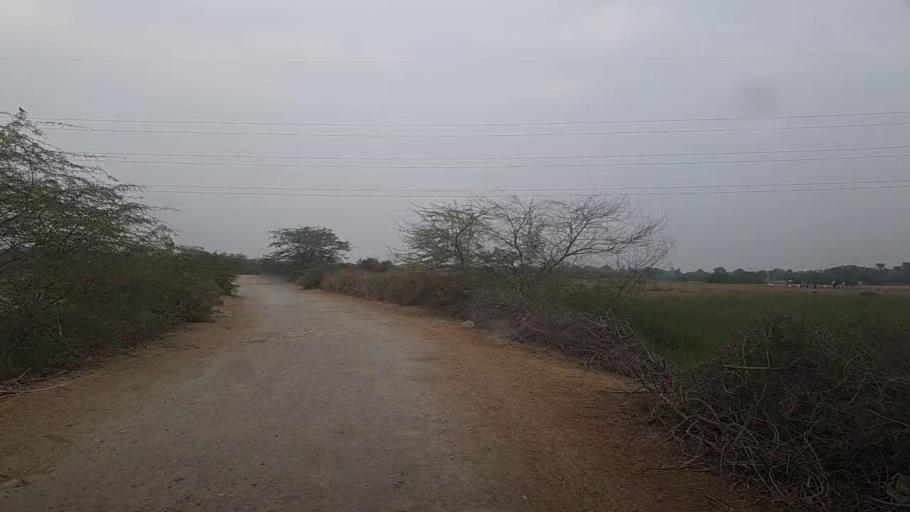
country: PK
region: Sindh
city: Gambat
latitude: 27.3424
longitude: 68.6019
